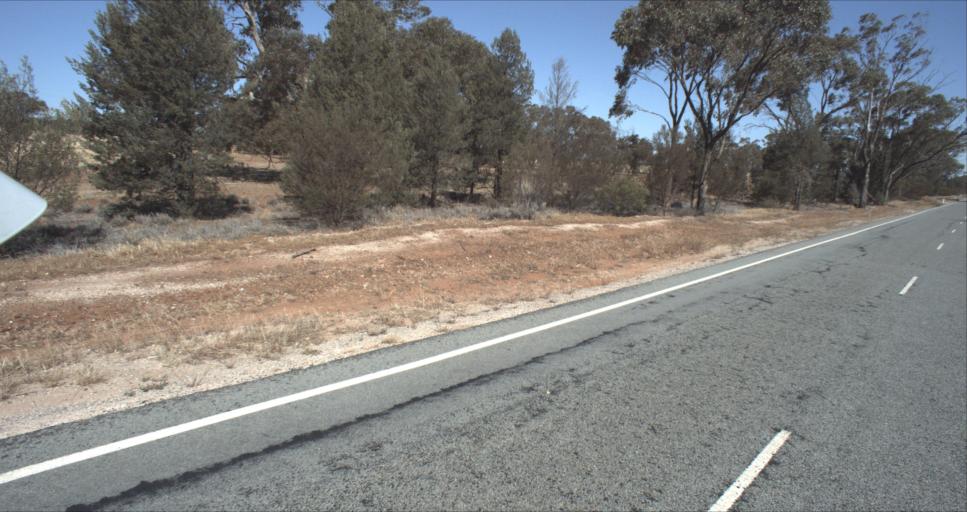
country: AU
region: New South Wales
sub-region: Leeton
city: Leeton
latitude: -34.4812
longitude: 146.4341
